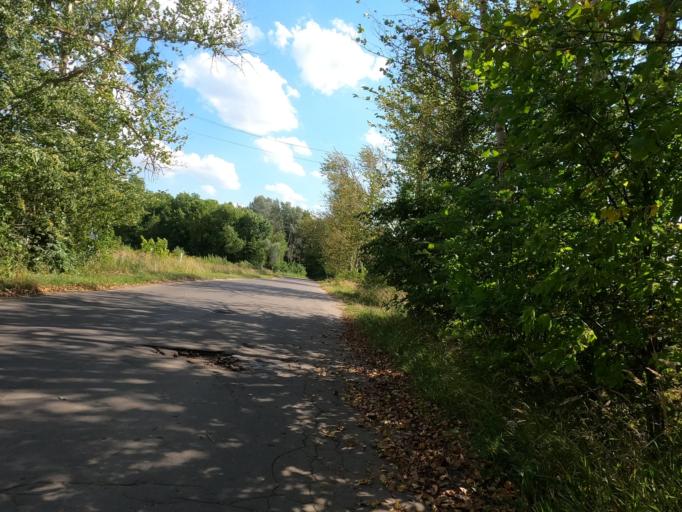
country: RU
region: Moskovskaya
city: Peski
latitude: 55.2238
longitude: 38.7521
